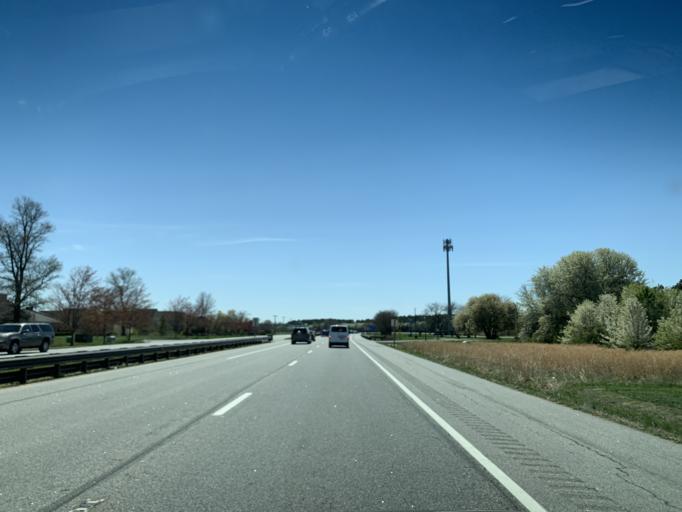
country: US
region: Maryland
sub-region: Talbot County
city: Easton
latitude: 38.7440
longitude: -76.0676
